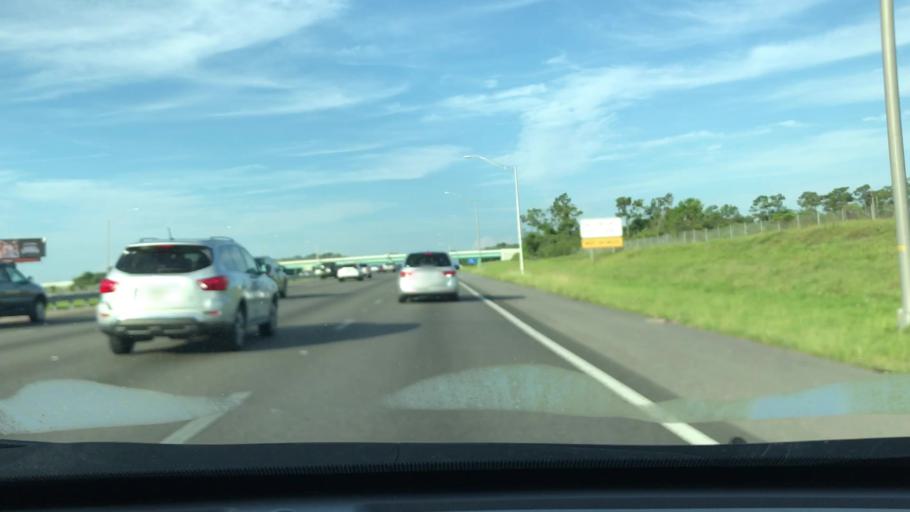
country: US
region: Florida
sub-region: Orange County
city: Williamsburg
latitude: 28.4008
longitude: -81.4846
